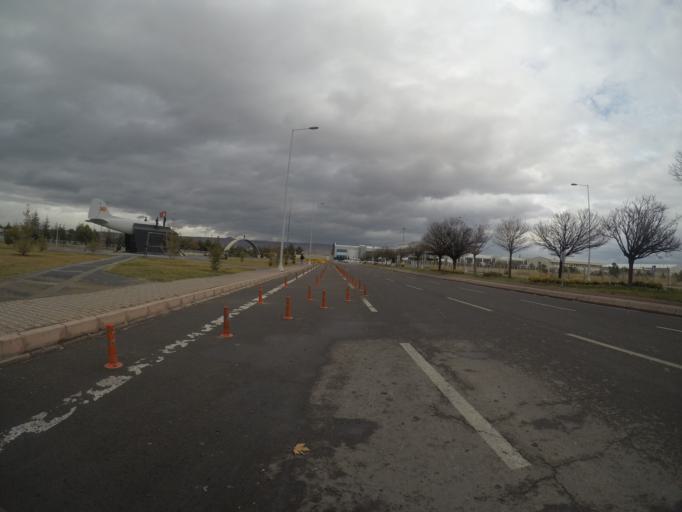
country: TR
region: Kayseri
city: Kayseri
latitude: 38.7631
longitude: 35.4815
